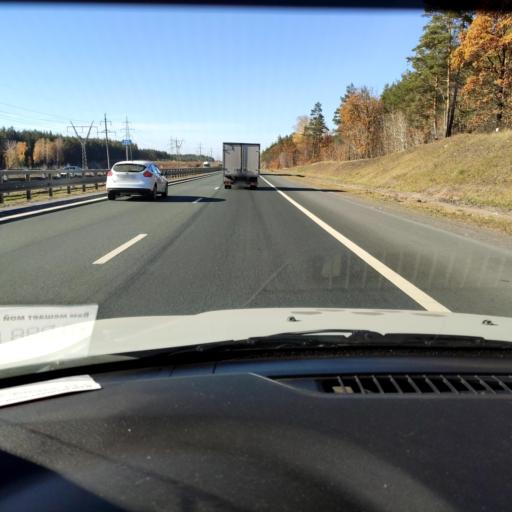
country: RU
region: Samara
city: Povolzhskiy
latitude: 53.5170
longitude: 49.7422
